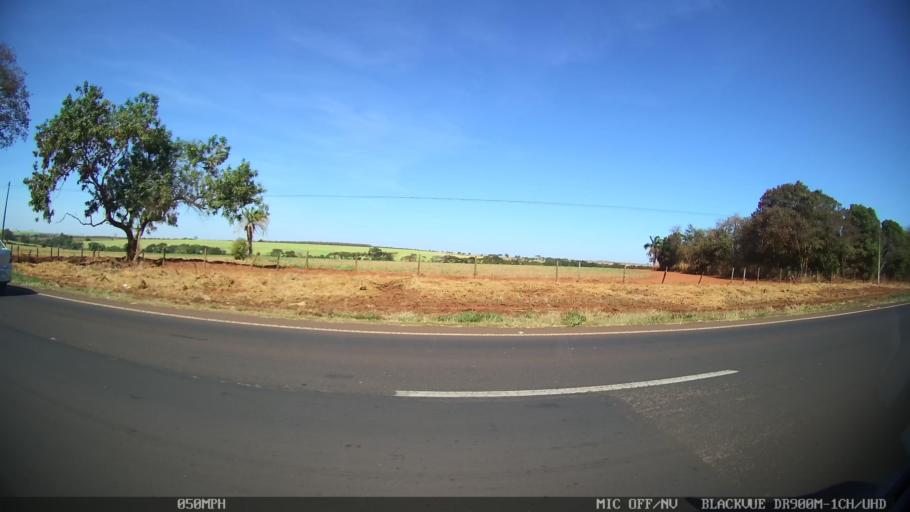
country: BR
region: Sao Paulo
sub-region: Barretos
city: Barretos
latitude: -20.5751
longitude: -48.6788
